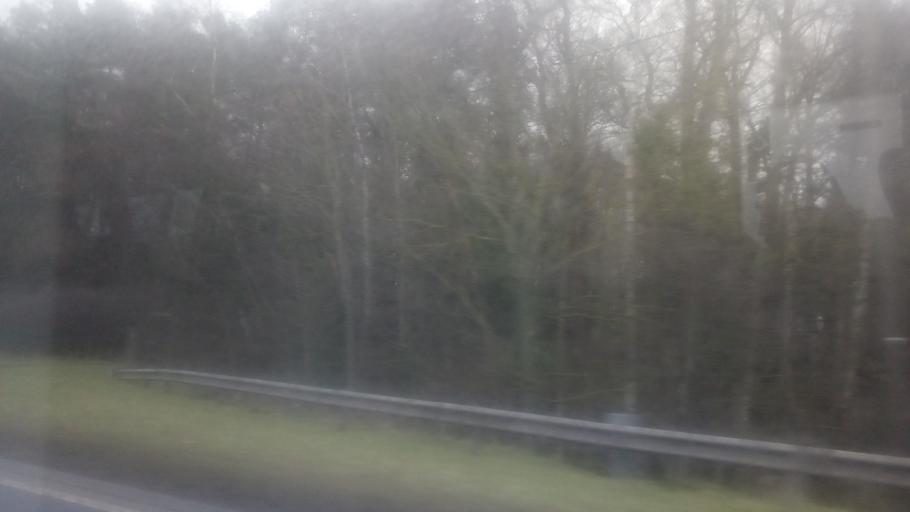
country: GB
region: Scotland
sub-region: The Scottish Borders
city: Newtown St Boswells
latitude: 55.5925
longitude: -2.6702
